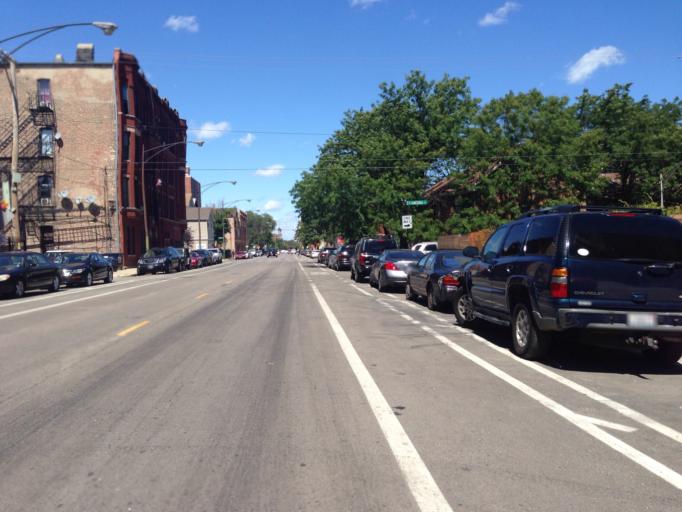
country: US
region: Illinois
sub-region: Cook County
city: Chicago
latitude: 41.8934
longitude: -87.6623
